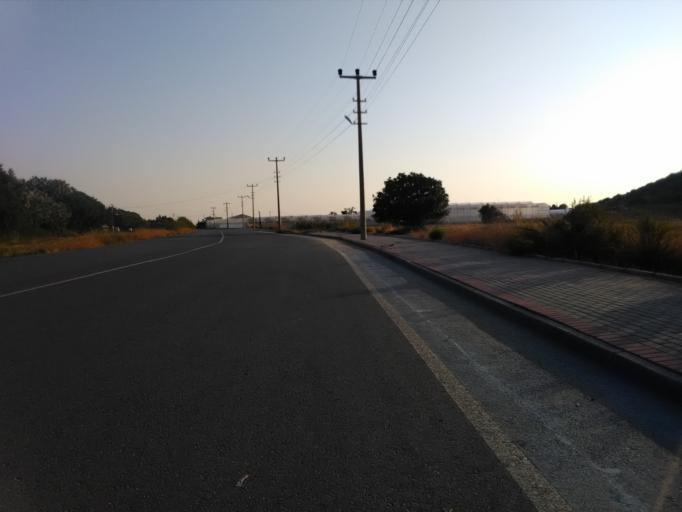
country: TR
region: Antalya
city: Gazipasa
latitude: 36.2584
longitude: 32.2902
